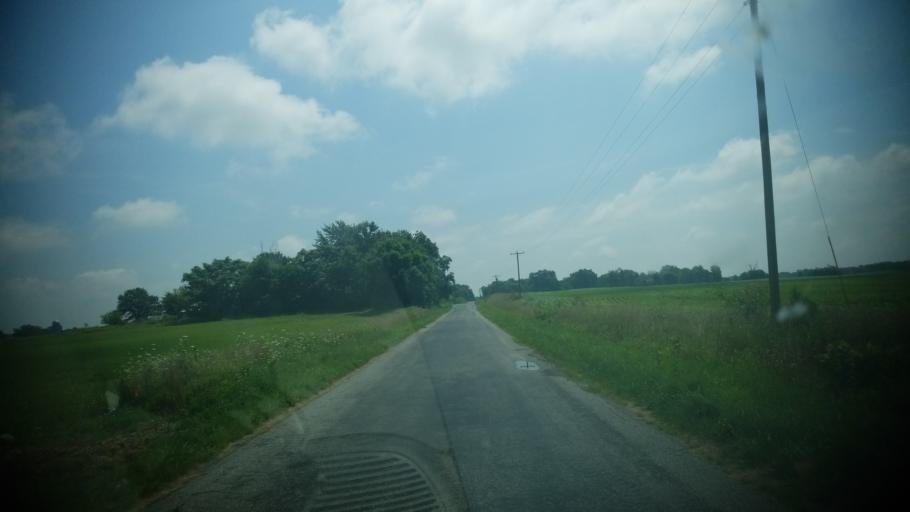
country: US
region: Illinois
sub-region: Wayne County
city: Fairfield
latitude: 38.5223
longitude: -88.3650
